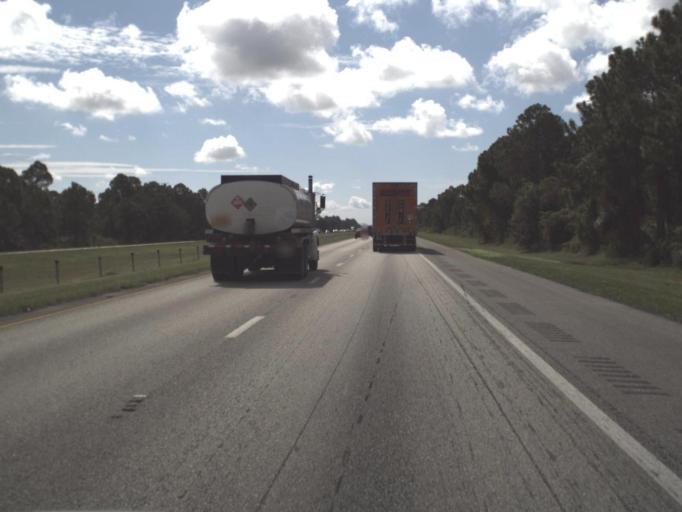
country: US
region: Florida
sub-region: Charlotte County
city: Port Charlotte
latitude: 27.0733
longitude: -82.1002
